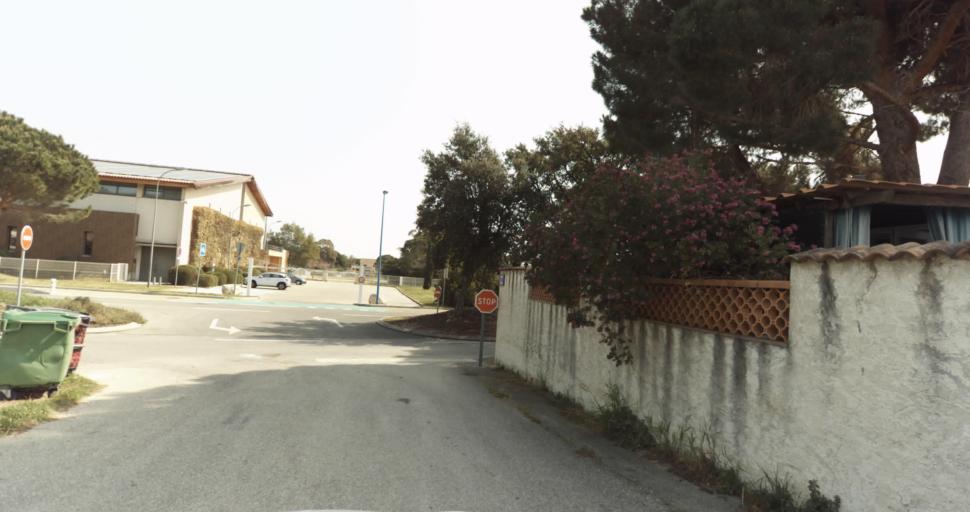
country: FR
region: Provence-Alpes-Cote d'Azur
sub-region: Departement du Var
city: Bormes-les-Mimosas
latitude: 43.1395
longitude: 6.3458
